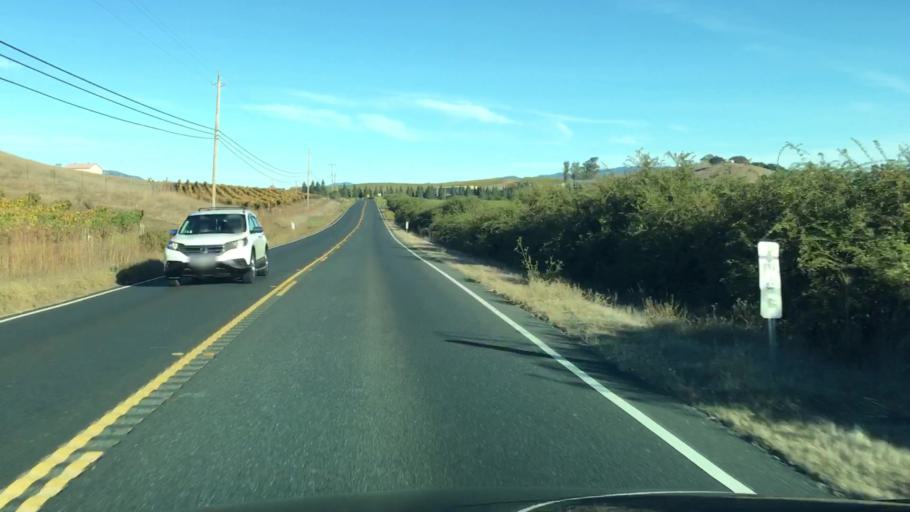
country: US
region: California
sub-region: Sonoma County
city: Temelec
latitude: 38.1960
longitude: -122.4453
